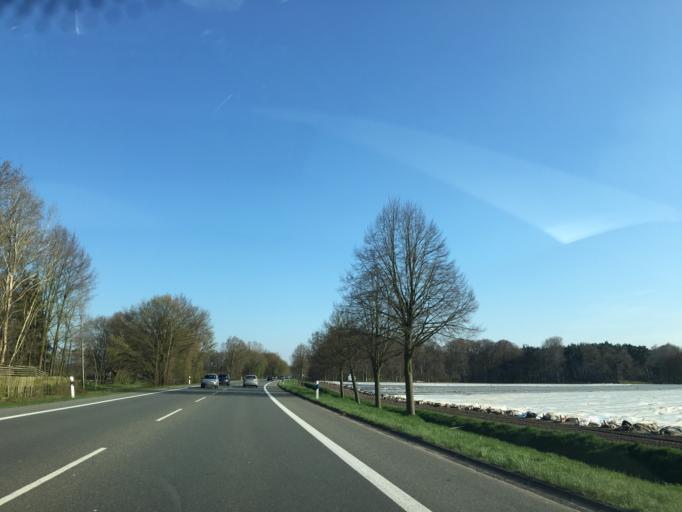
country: DE
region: North Rhine-Westphalia
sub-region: Regierungsbezirk Munster
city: Greven
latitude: 52.0654
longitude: 7.6688
